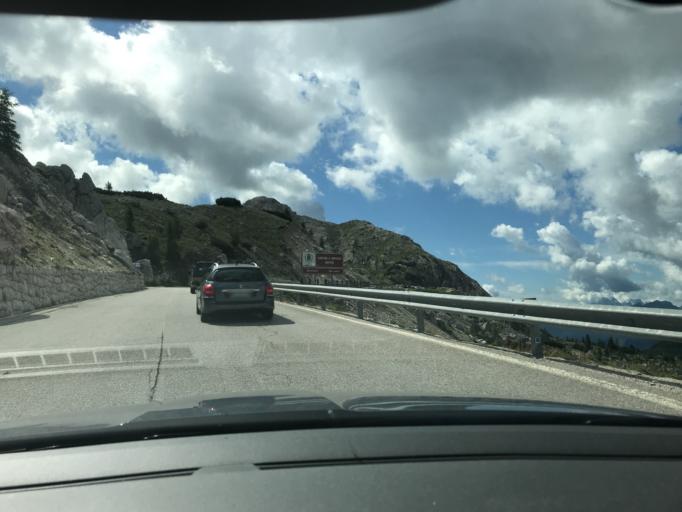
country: IT
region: Veneto
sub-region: Provincia di Belluno
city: Livinallongo del Col di Lana
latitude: 46.5318
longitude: 11.9890
